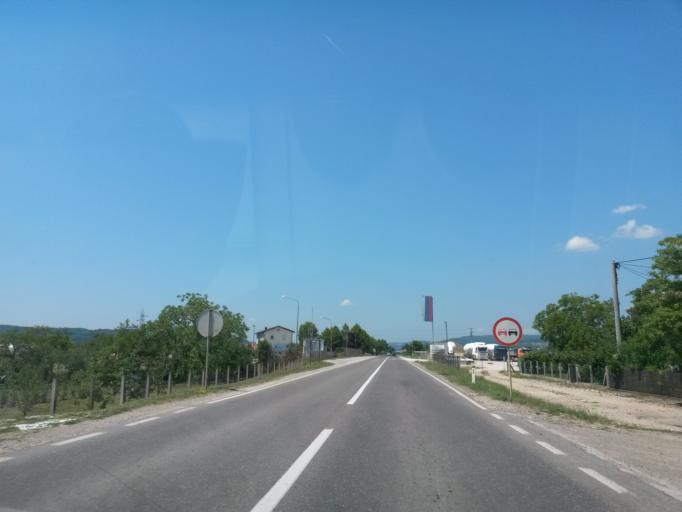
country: BA
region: Federation of Bosnia and Herzegovina
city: Odzak
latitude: 44.9645
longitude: 18.3266
